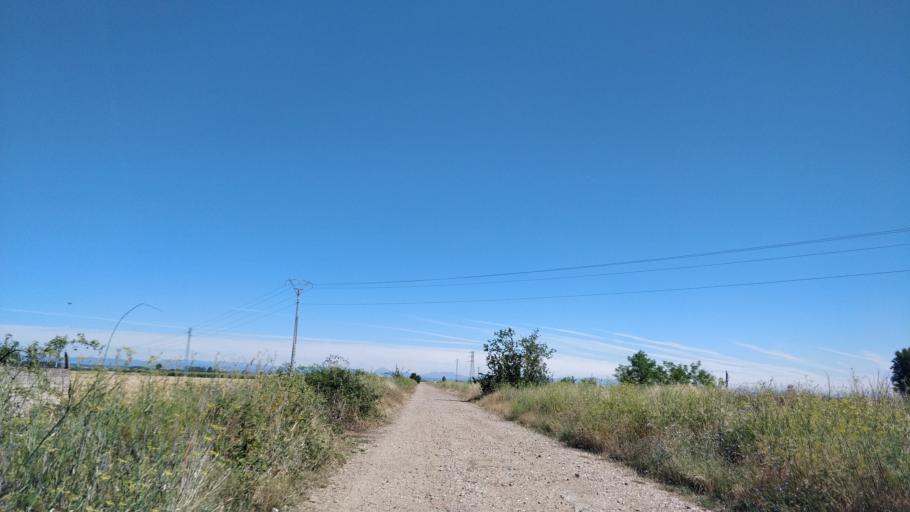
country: ES
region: Castille and Leon
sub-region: Provincia de Leon
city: Bustillo del Paramo
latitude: 42.4257
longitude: -5.8212
